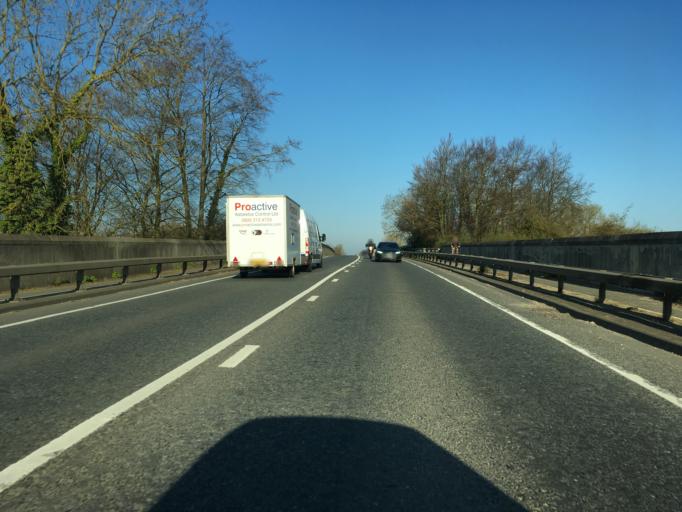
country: GB
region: England
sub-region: Oxfordshire
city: Yarnton
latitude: 51.7909
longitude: -1.2922
